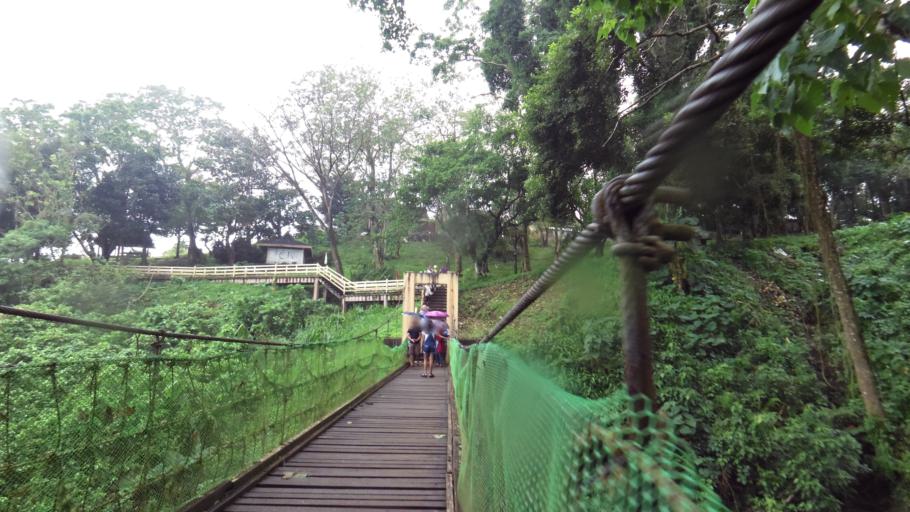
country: PH
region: Calabarzon
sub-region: Province of Cavite
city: Patuto
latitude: 14.1242
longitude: 120.9992
